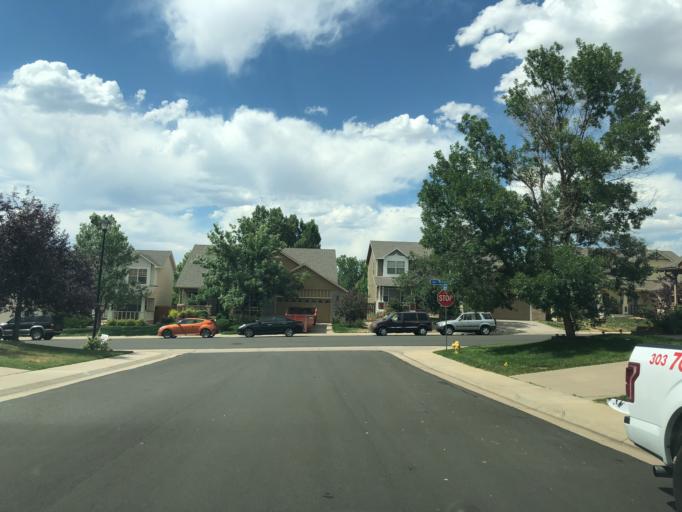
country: US
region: Colorado
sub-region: Arapahoe County
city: Dove Valley
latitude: 39.6212
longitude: -104.7702
